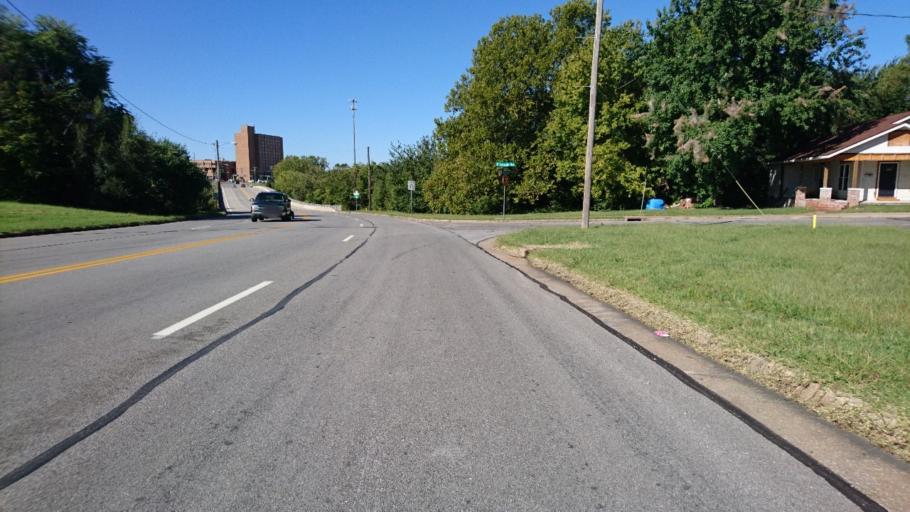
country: US
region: Missouri
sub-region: Jasper County
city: Joplin
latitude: 37.0919
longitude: -94.5078
